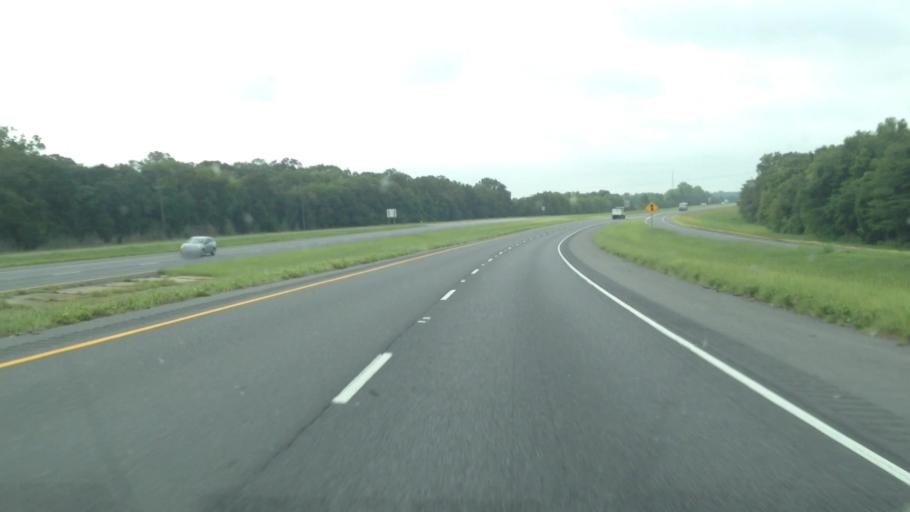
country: US
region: Louisiana
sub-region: Saint Landry Parish
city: Opelousas
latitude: 30.6406
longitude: -92.0493
